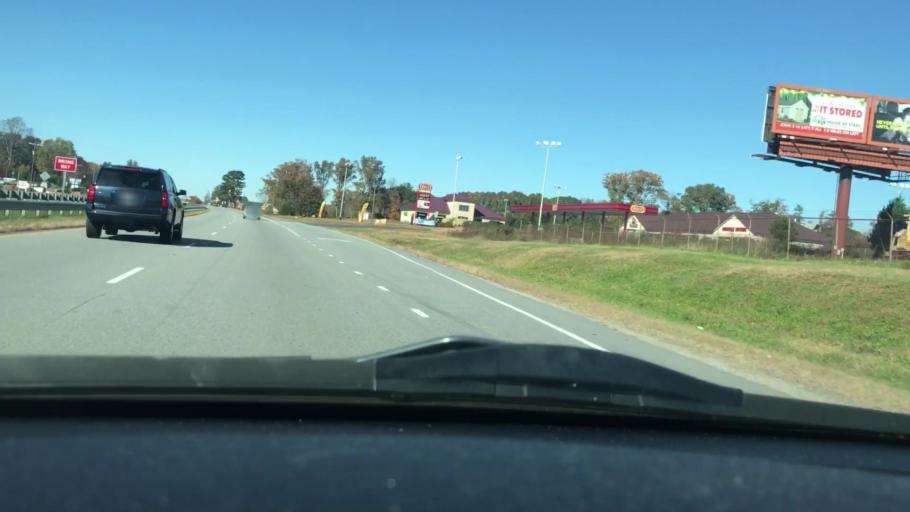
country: US
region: North Carolina
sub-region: Rockingham County
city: Madison
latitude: 36.3093
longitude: -79.9417
